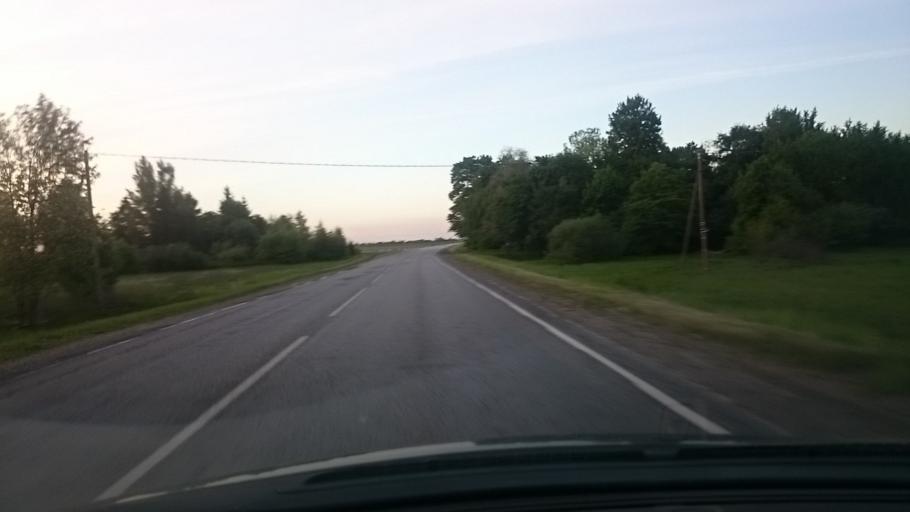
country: EE
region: Viljandimaa
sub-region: Vohma linn
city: Vohma
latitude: 58.6389
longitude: 25.5759
